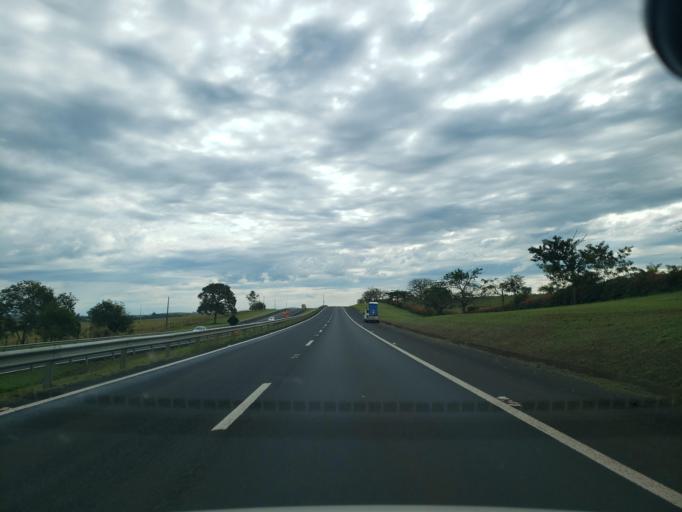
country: BR
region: Sao Paulo
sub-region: Bauru
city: Bauru
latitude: -22.2167
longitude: -49.1703
